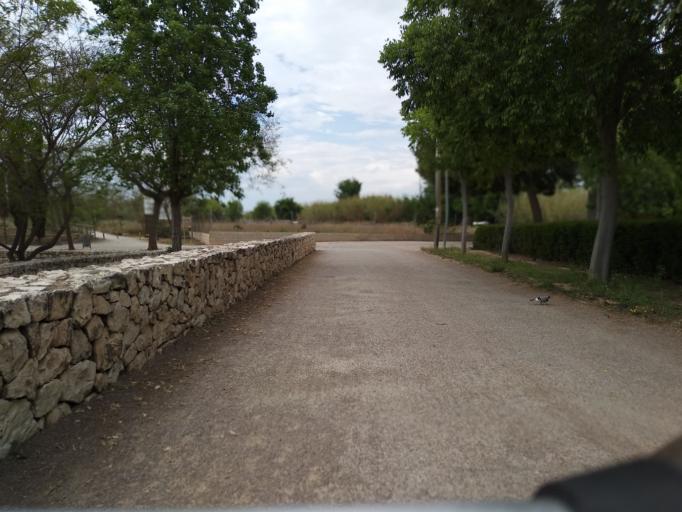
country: ES
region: Valencia
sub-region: Provincia de Valencia
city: Mislata
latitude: 39.4813
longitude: -0.4099
